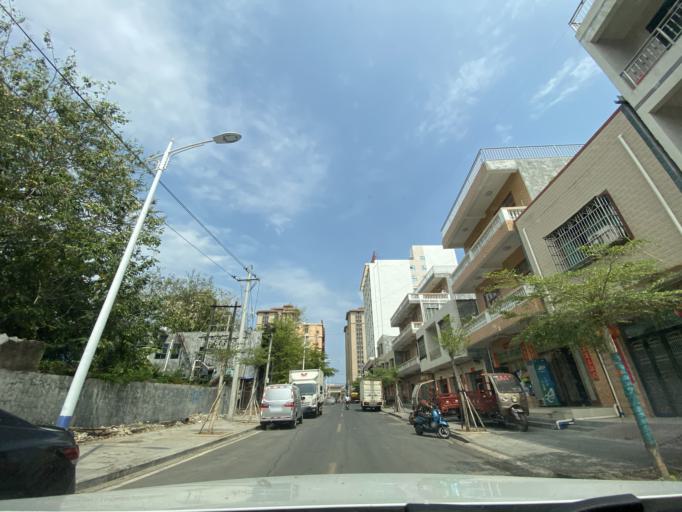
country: CN
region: Hainan
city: Yingzhou
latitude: 18.4252
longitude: 109.8537
